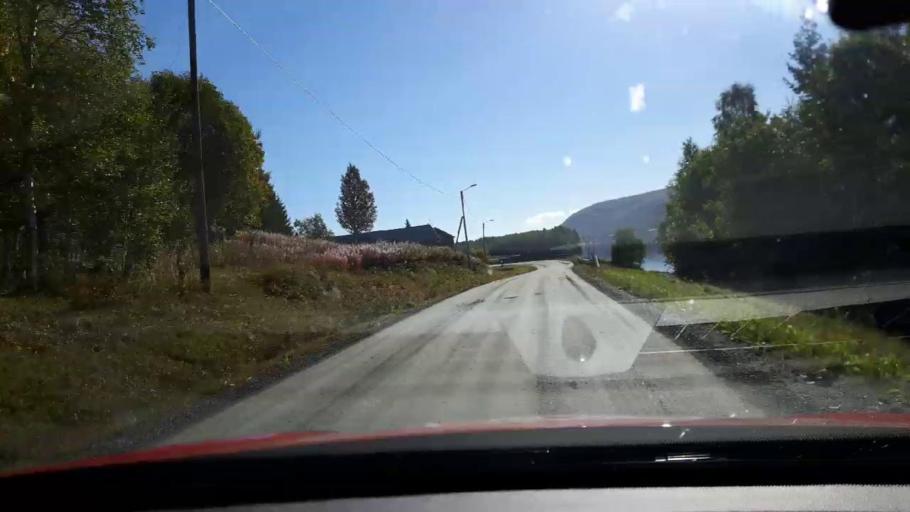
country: NO
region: Nord-Trondelag
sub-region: Lierne
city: Sandvika
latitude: 64.6465
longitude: 13.7647
